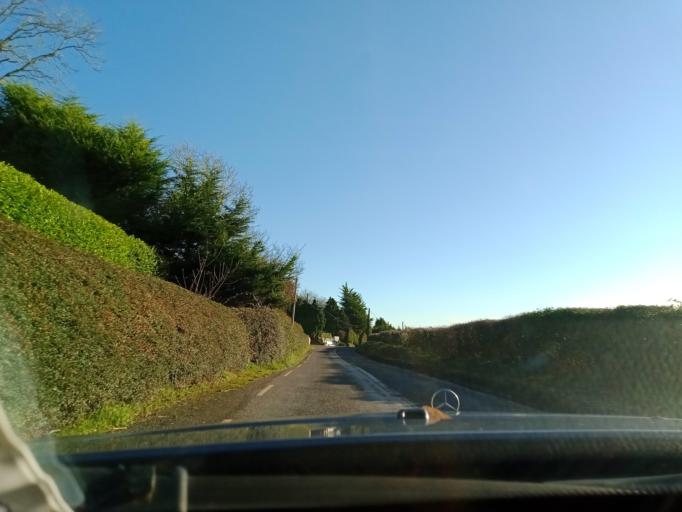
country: IE
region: Leinster
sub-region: Kilkenny
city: Piltown
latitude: 52.3948
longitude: -7.3631
